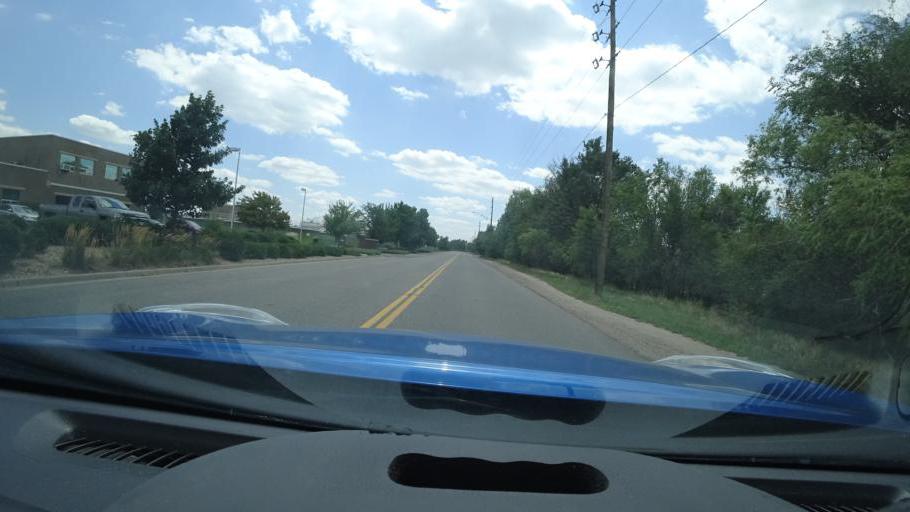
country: US
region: Colorado
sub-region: Arapahoe County
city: Englewood
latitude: 39.6645
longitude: -105.0041
